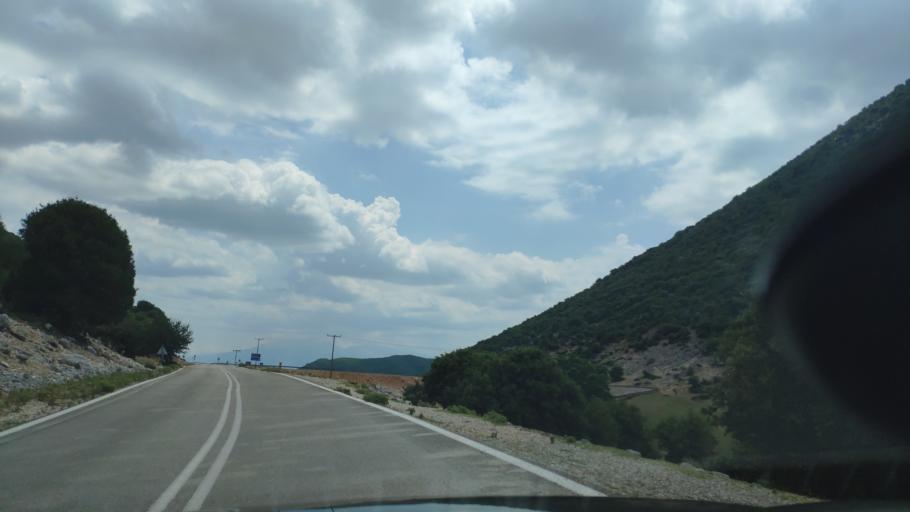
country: GR
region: Epirus
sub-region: Nomos Artas
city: Kampi
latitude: 39.2754
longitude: 20.9624
